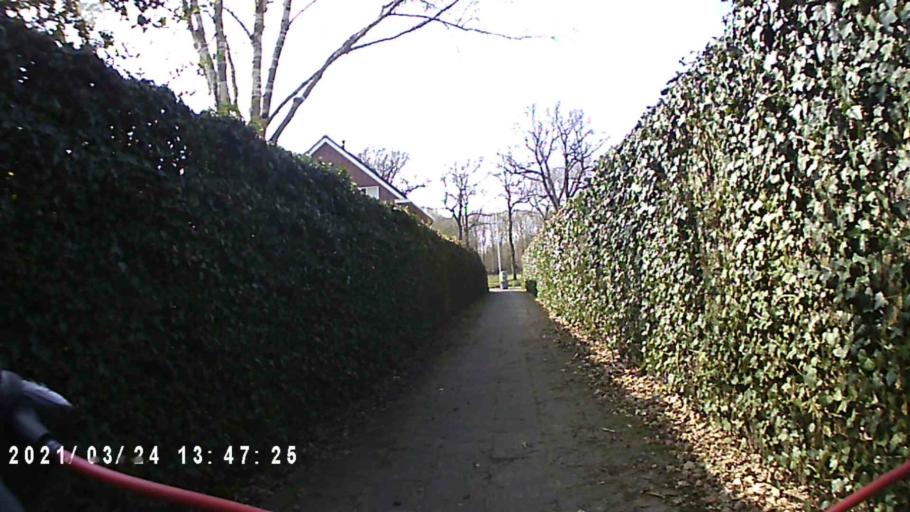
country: NL
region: Friesland
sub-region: Gemeente Smallingerland
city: Drachtstercompagnie
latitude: 53.0794
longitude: 6.2593
